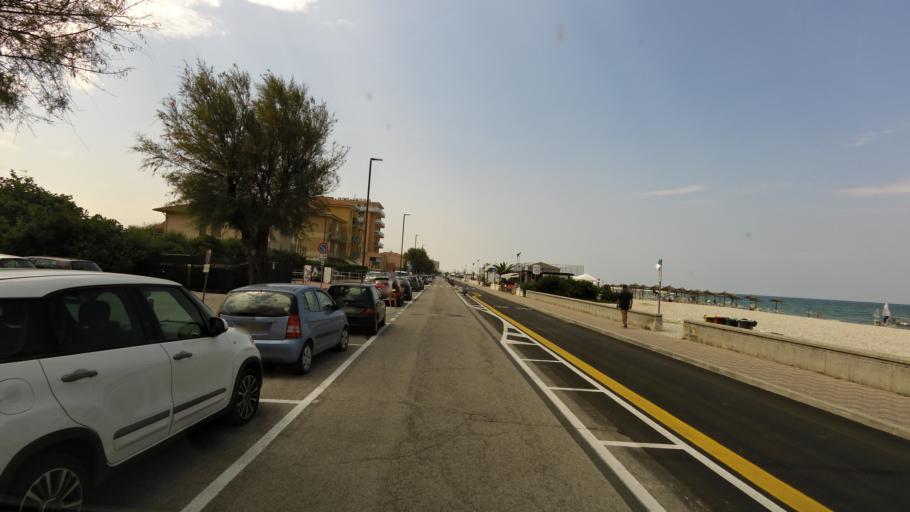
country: IT
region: The Marches
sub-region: Provincia di Pesaro e Urbino
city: Marotta
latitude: 43.7653
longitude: 13.1468
